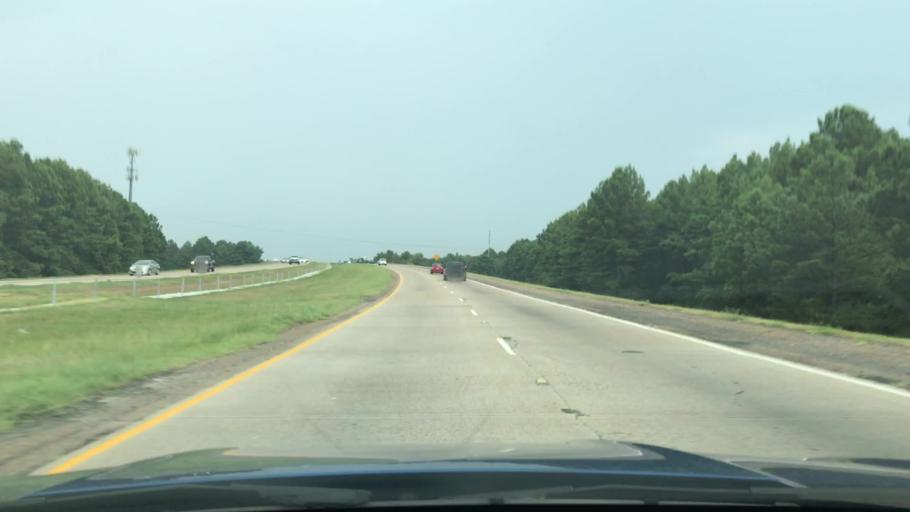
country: US
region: Louisiana
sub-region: Caddo Parish
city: Shreveport
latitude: 32.4215
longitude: -93.8342
